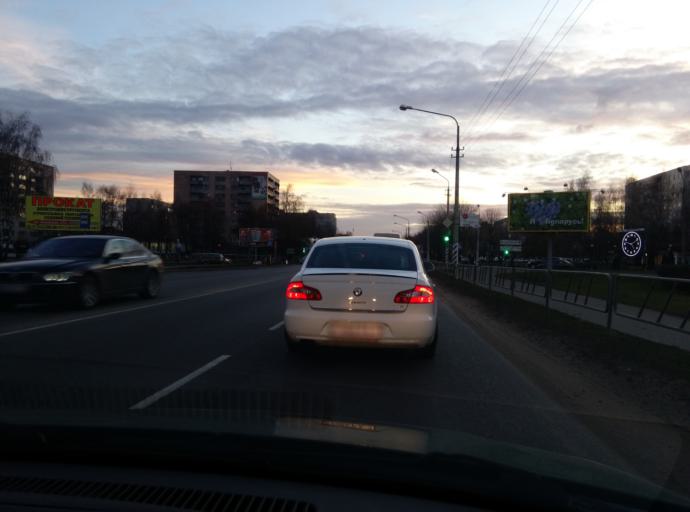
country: BY
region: Minsk
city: Horad Barysaw
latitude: 54.2202
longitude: 28.4917
